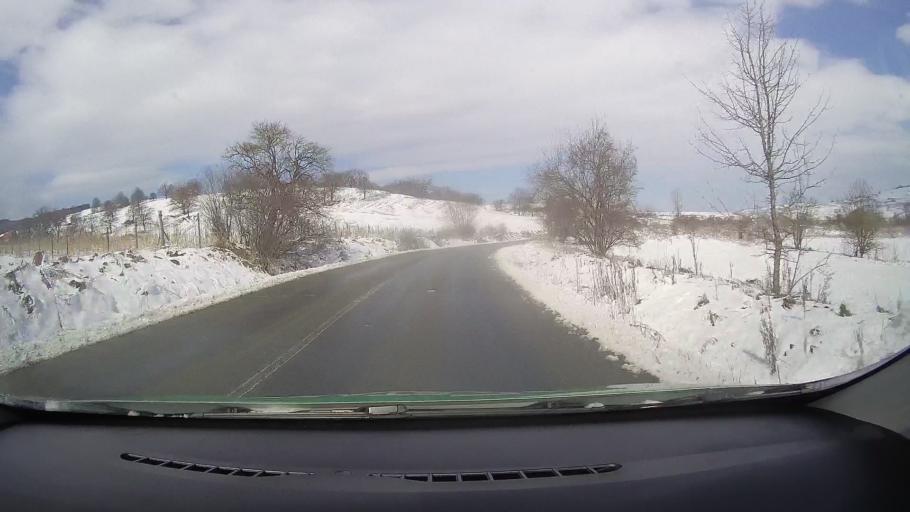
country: RO
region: Sibiu
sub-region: Comuna Altina
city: Altina
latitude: 45.9469
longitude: 24.4506
